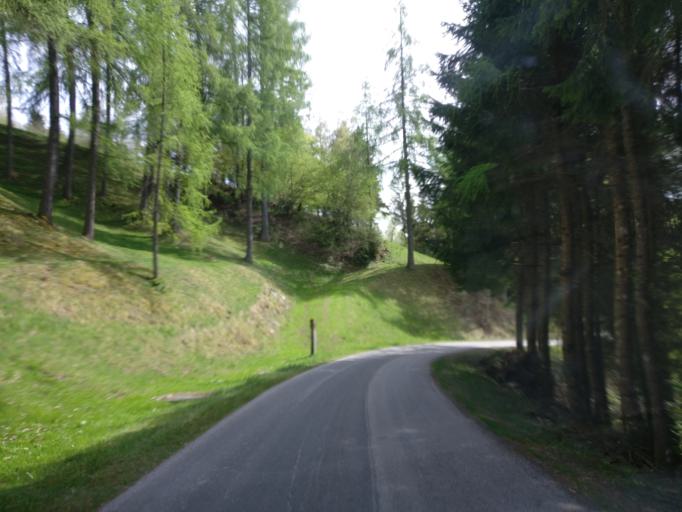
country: AT
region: Salzburg
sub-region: Politischer Bezirk Sankt Johann im Pongau
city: Pfarrwerfen
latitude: 47.4799
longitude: 13.2090
